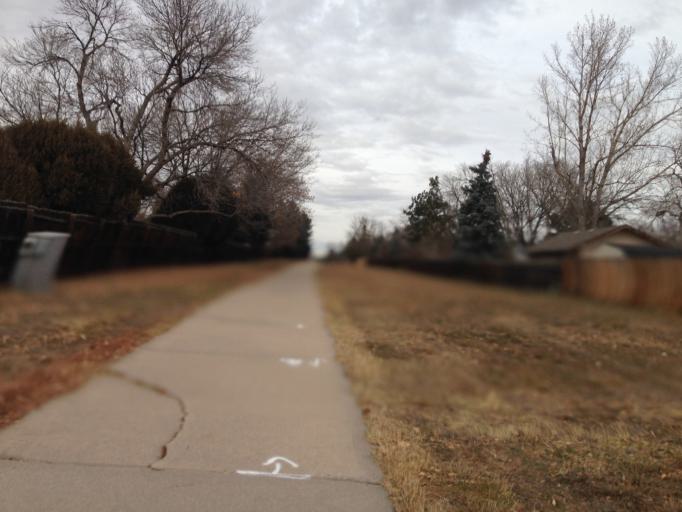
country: US
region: Colorado
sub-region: Adams County
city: Westminster
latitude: 39.8500
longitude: -105.0627
